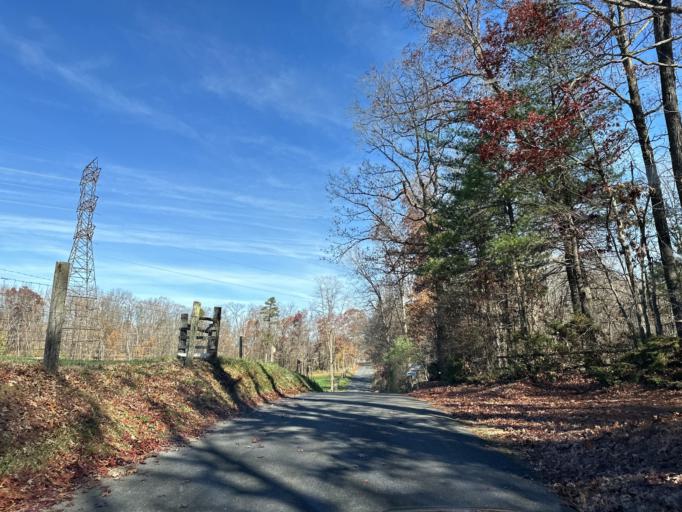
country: US
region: Virginia
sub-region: Augusta County
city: Weyers Cave
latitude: 38.3206
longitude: -78.9644
